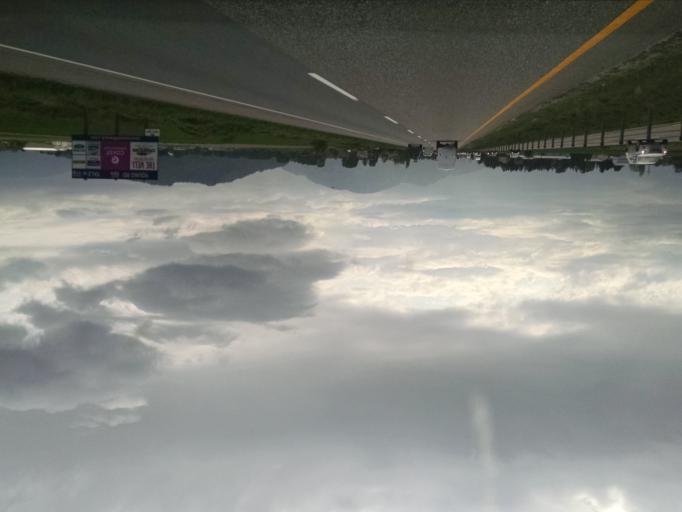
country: CA
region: British Columbia
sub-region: Fraser Valley Regional District
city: Chilliwack
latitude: 49.1531
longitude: -121.9290
